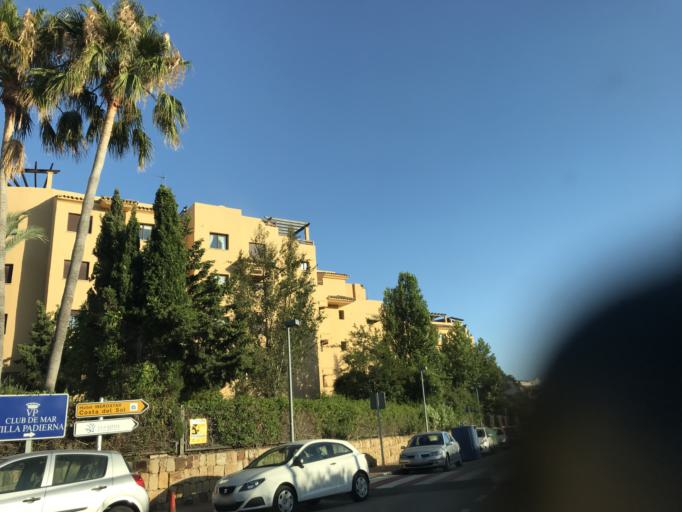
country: ES
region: Andalusia
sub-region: Provincia de Malaga
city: Benahavis
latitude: 36.4588
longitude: -5.0470
